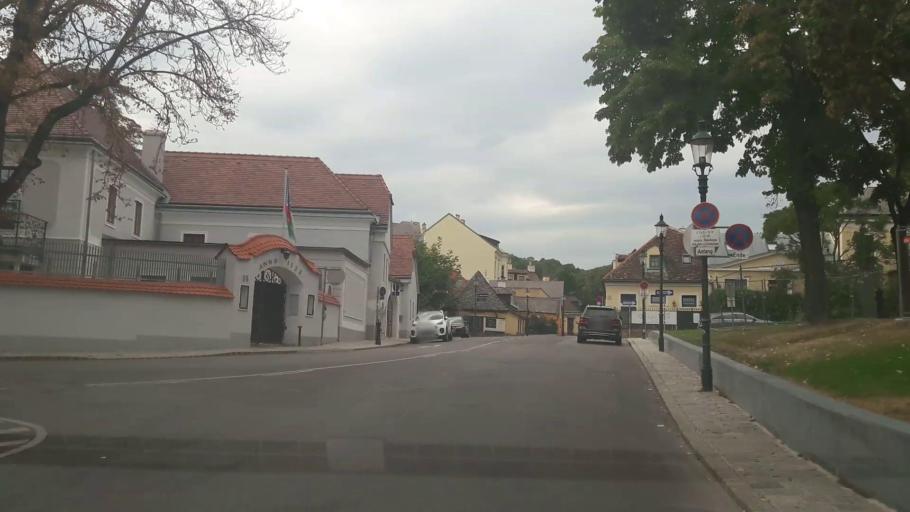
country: AT
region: Lower Austria
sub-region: Politischer Bezirk Korneuburg
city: Langenzersdorf
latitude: 48.2581
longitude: 16.3378
